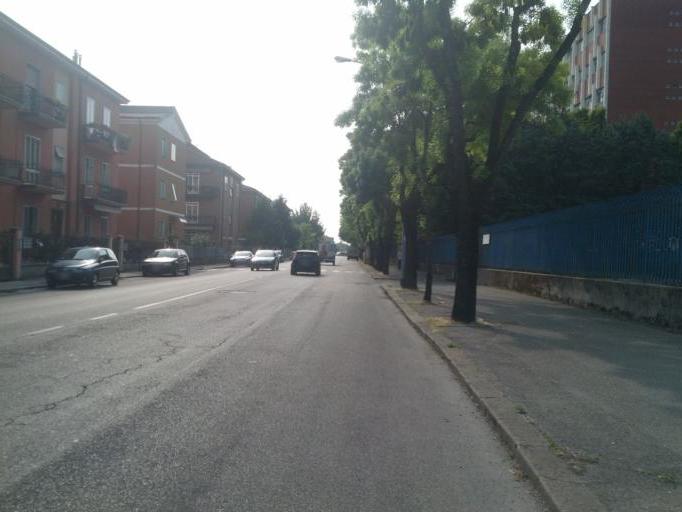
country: IT
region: Veneto
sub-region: Provincia di Verona
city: Montorio
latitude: 45.4389
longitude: 11.0395
